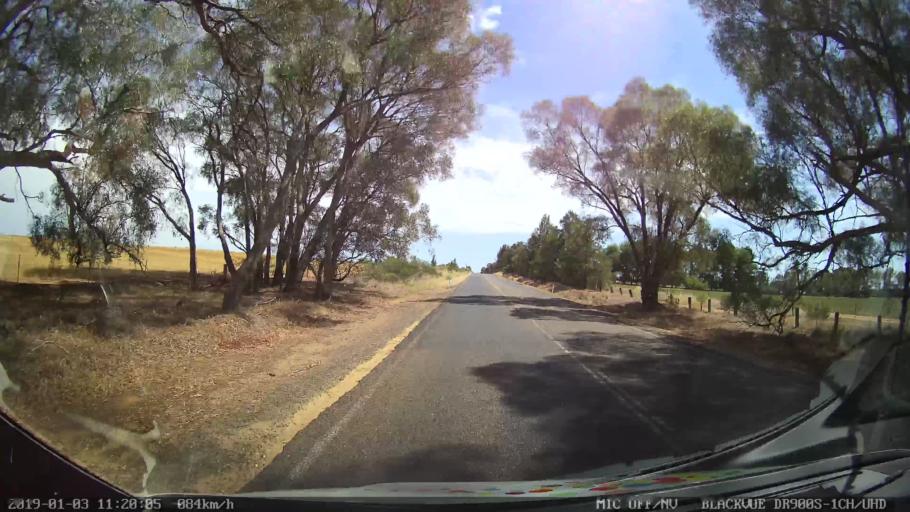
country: AU
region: New South Wales
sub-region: Young
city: Young
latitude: -34.1054
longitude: 148.2552
